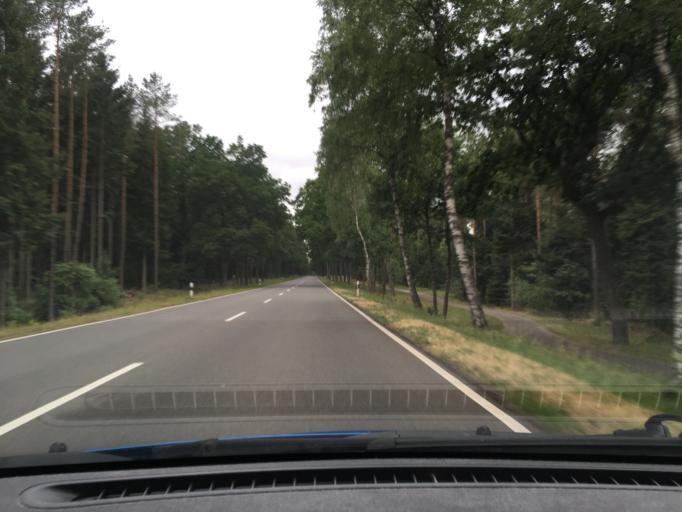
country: DE
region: Lower Saxony
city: Bispingen
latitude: 53.0816
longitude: 9.9535
